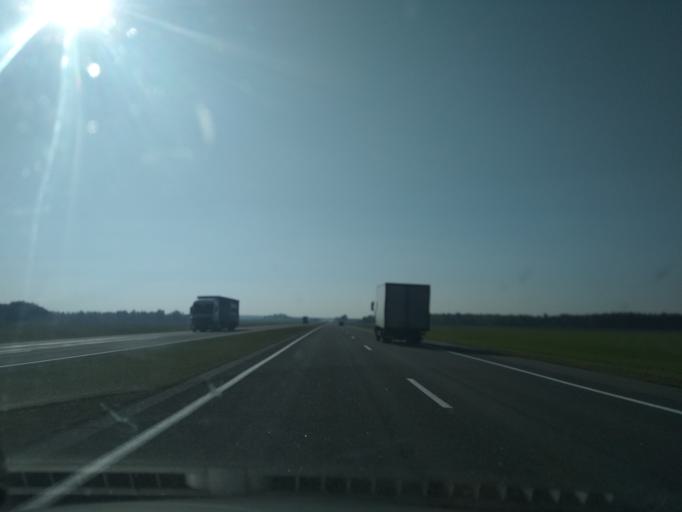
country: BY
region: Brest
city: Antopal'
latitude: 52.3194
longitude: 24.6151
